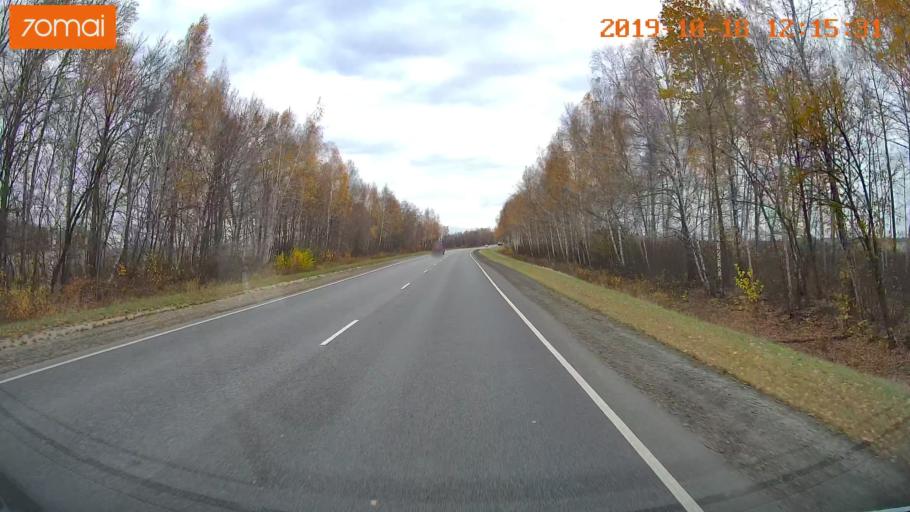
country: RU
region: Rjazan
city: Zakharovo
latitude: 54.4441
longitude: 39.4008
